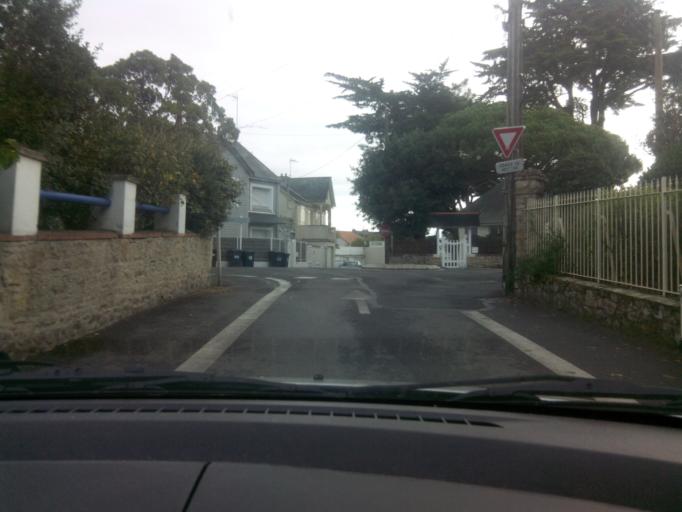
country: FR
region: Pays de la Loire
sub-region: Departement de la Loire-Atlantique
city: Pornichet
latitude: 47.2689
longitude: -2.3460
